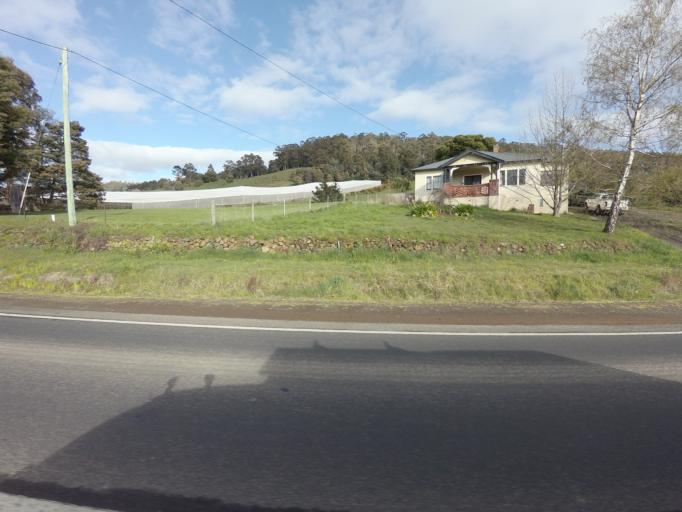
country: AU
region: Tasmania
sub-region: Huon Valley
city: Franklin
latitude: -43.0786
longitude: 147.0173
